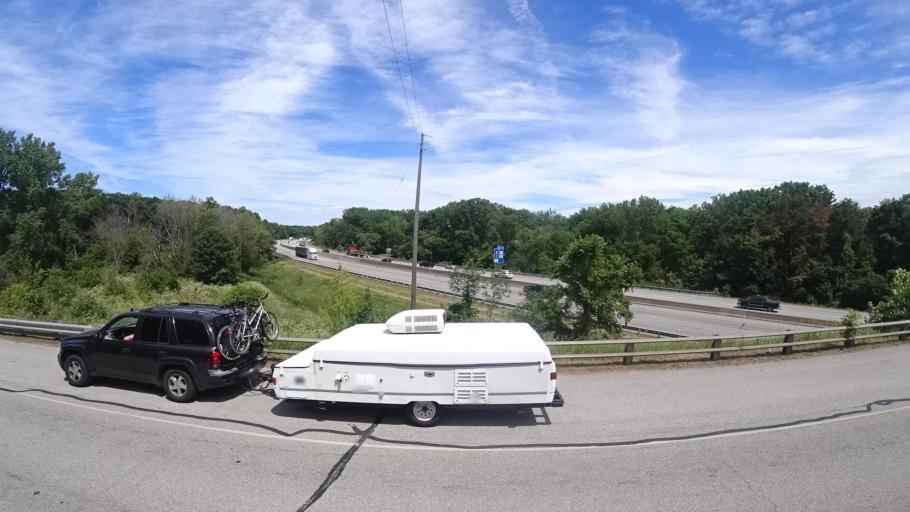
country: US
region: Indiana
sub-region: Porter County
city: Porter
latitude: 41.6213
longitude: -87.0771
